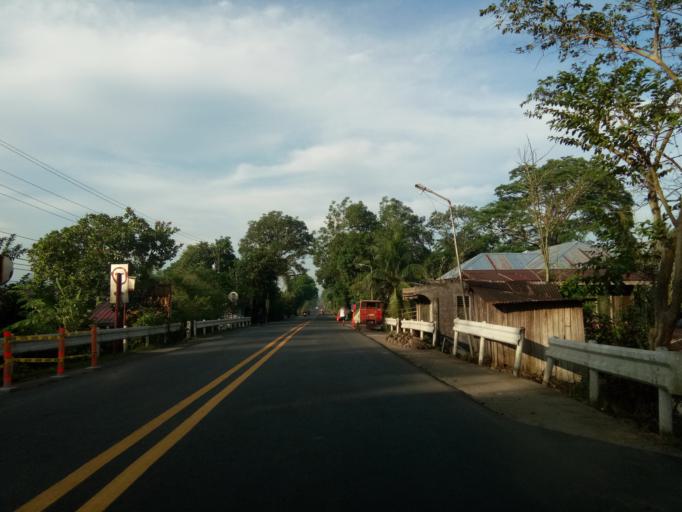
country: PH
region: Caraga
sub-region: Province of Surigao del Norte
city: Tubod
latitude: 9.5540
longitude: 125.5682
